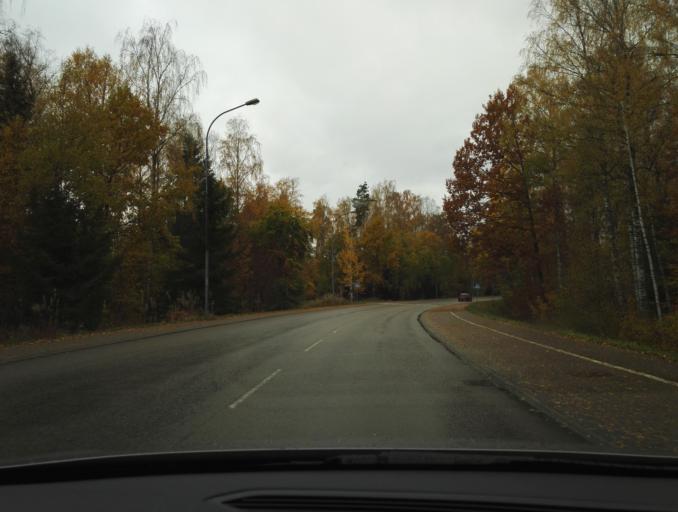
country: SE
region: Kronoberg
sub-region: Vaxjo Kommun
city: Vaexjoe
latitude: 56.8926
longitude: 14.7400
